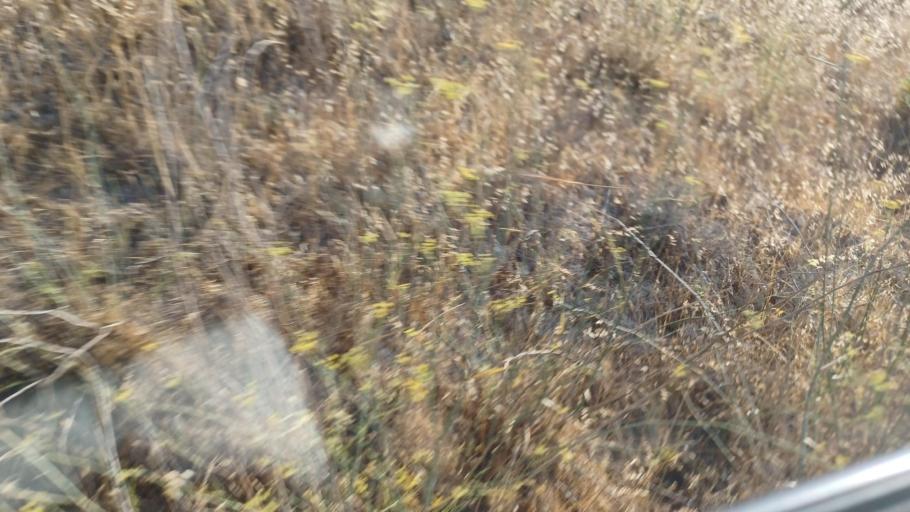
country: CY
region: Pafos
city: Tala
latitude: 34.8965
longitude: 32.4521
